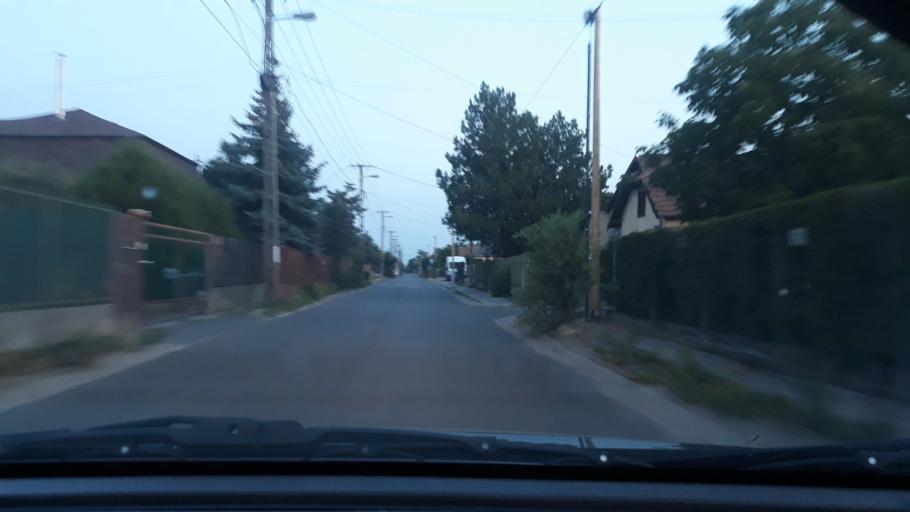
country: HU
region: Hajdu-Bihar
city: Debrecen
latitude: 47.5375
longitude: 21.6660
